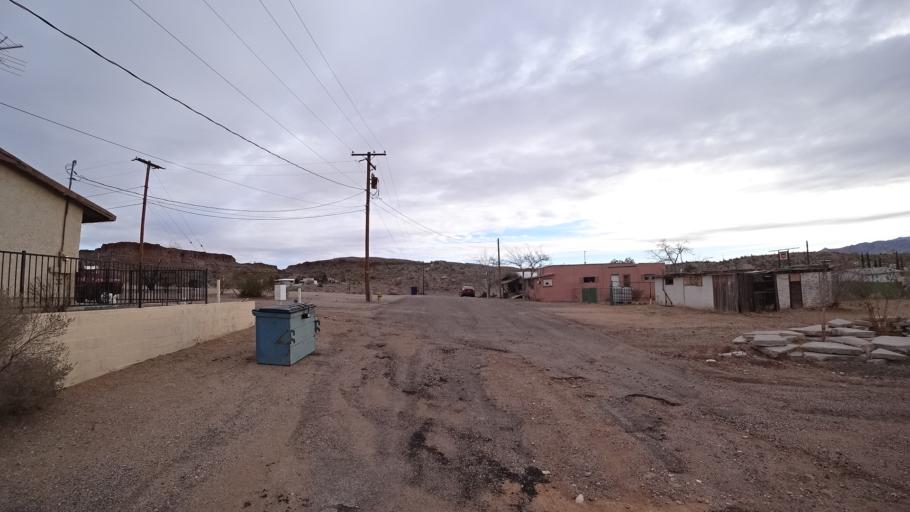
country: US
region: Arizona
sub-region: Mohave County
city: Kingman
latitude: 35.1971
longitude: -114.0776
